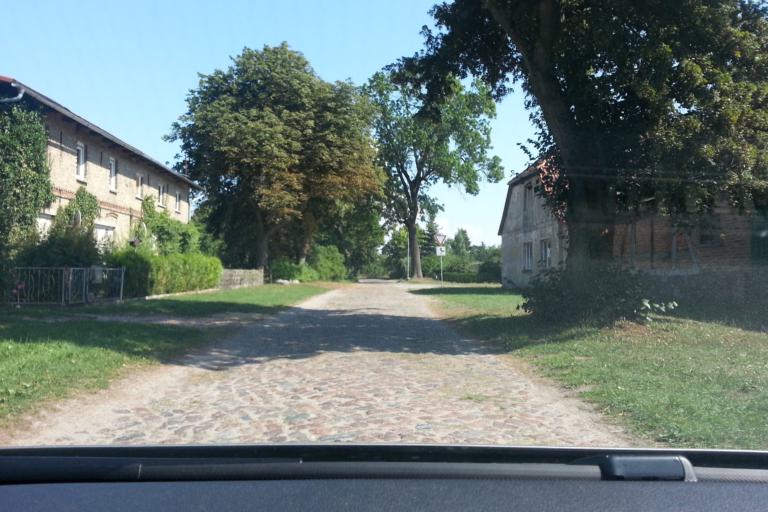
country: DE
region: Mecklenburg-Vorpommern
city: Ducherow
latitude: 53.7141
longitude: 13.7886
